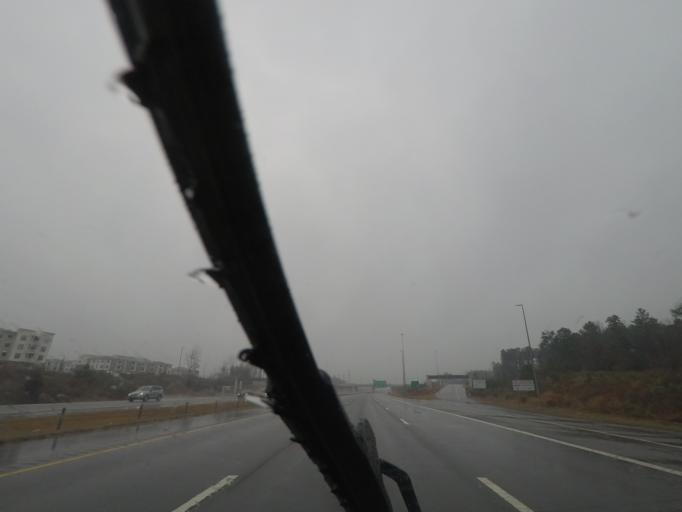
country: US
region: North Carolina
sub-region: Wake County
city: Morrisville
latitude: 35.8808
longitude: -78.8681
